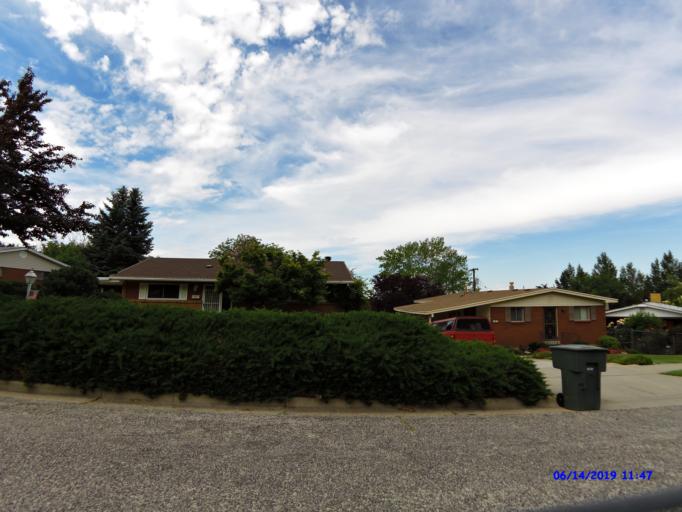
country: US
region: Utah
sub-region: Weber County
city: Ogden
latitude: 41.2548
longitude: -111.9403
